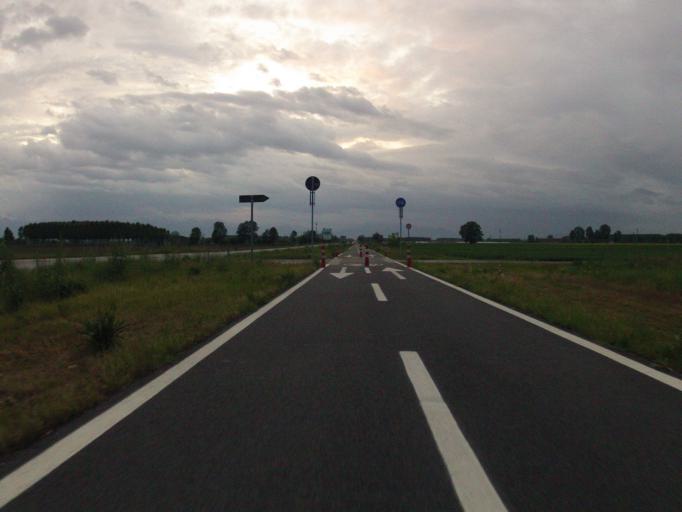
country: IT
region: Piedmont
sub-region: Provincia di Cuneo
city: Moretta
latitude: 44.7692
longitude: 7.5280
